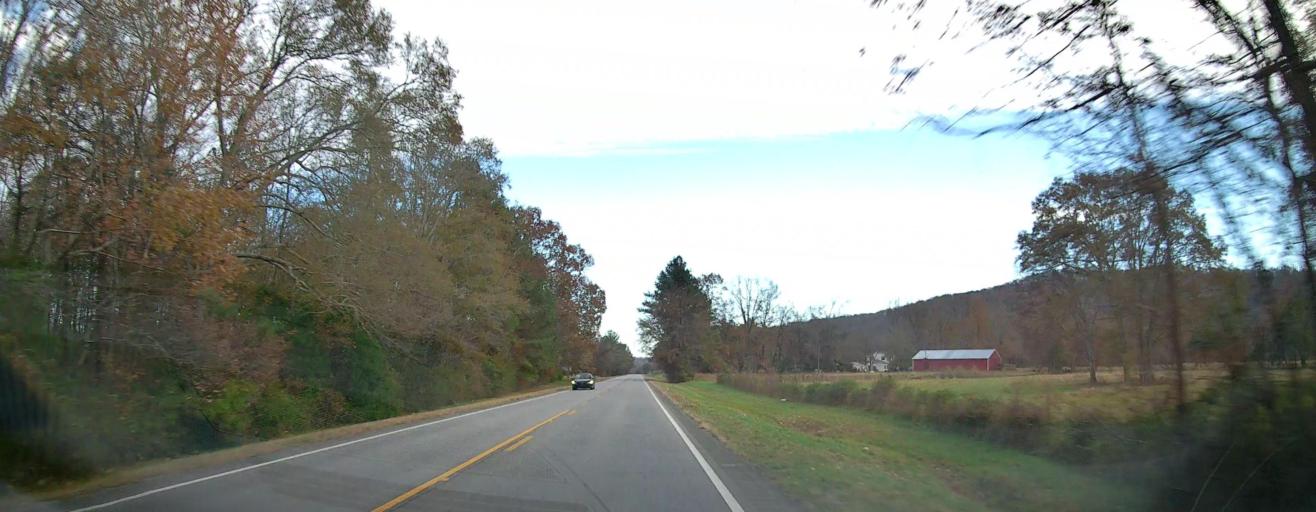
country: US
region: Alabama
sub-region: Marshall County
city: Arab
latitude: 34.3945
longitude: -86.6751
